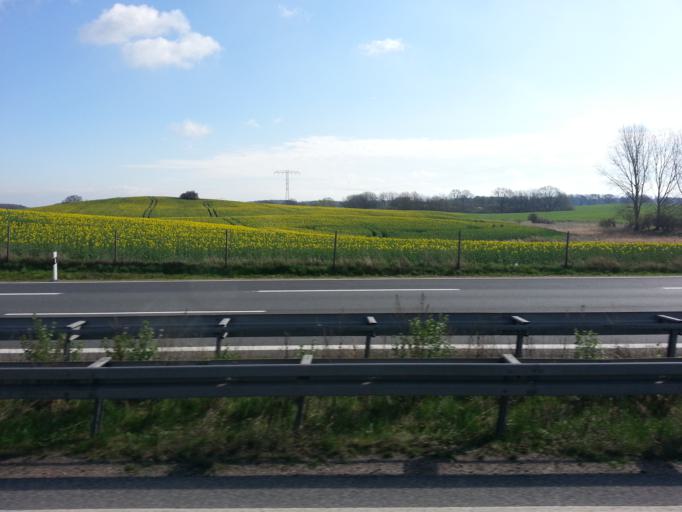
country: DE
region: Mecklenburg-Vorpommern
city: Lalendorf
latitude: 53.7081
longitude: 12.3577
